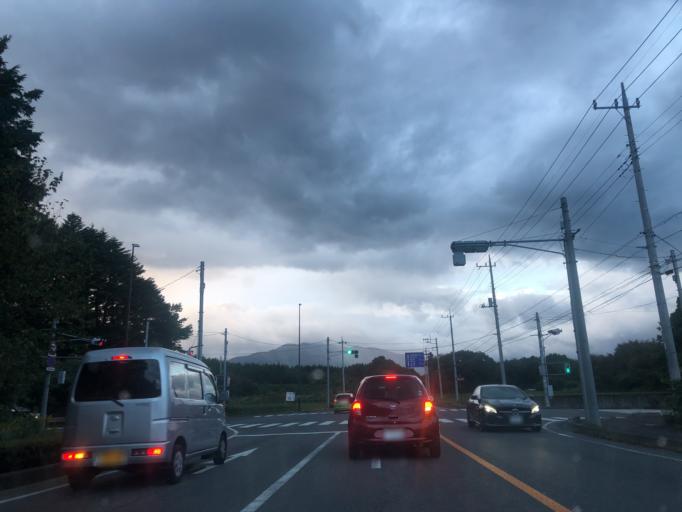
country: JP
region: Tochigi
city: Kuroiso
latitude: 36.9655
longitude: 139.9883
